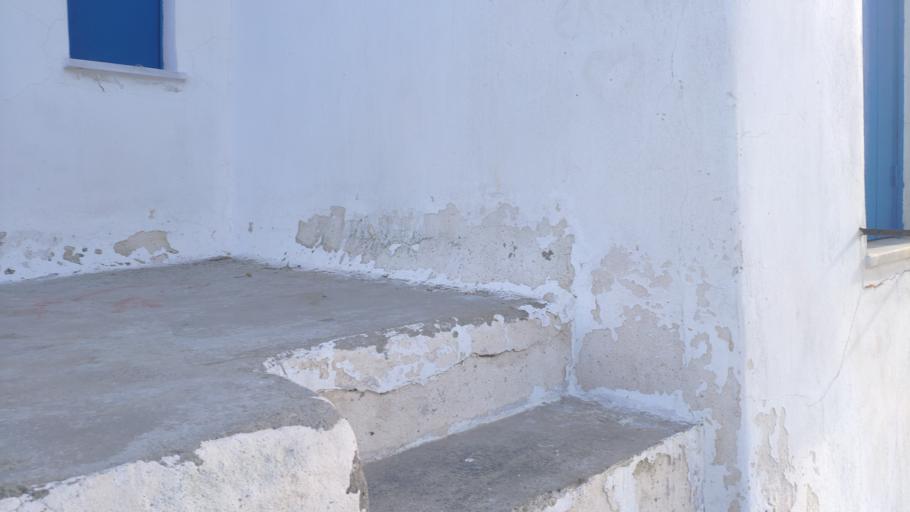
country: GR
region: Attica
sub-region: Nomarchia Dytikis Attikis
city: Nea Peramos
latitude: 37.9854
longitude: 23.4359
